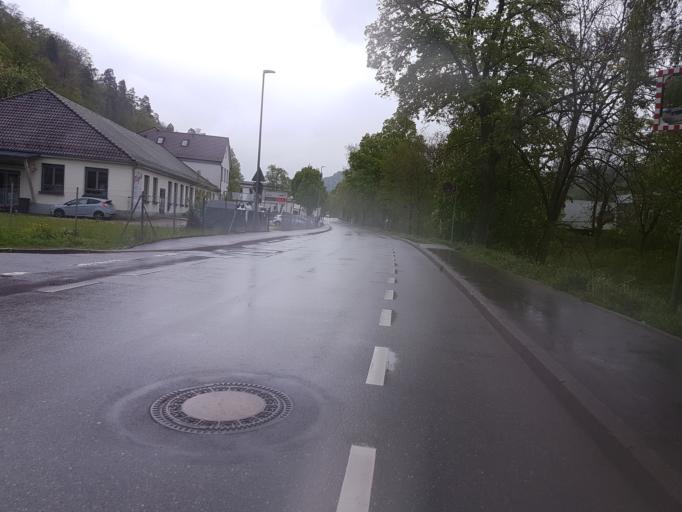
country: DE
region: Baden-Wuerttemberg
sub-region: Freiburg Region
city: Oberndorf
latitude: 48.2900
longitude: 8.5784
